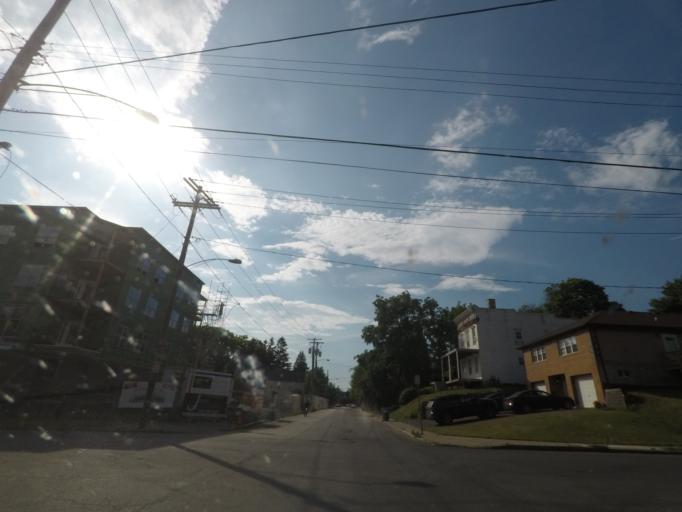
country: US
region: New York
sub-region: Albany County
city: West Albany
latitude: 42.6582
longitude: -73.7843
